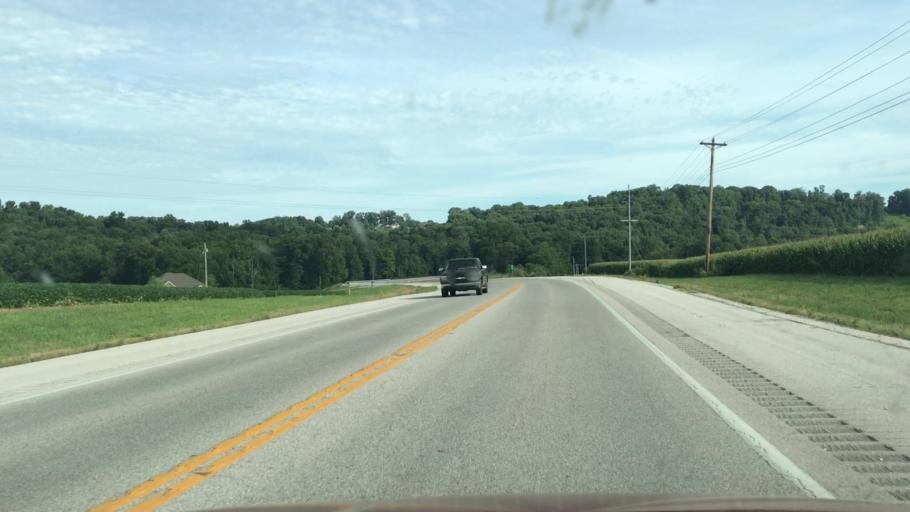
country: US
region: Kentucky
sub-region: Edmonson County
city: Brownsville
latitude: 37.0895
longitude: -86.2308
